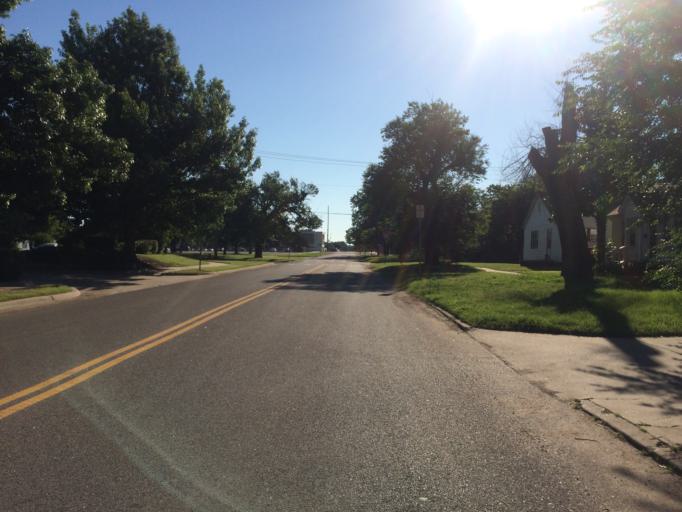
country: US
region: Oklahoma
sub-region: Cleveland County
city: Norman
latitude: 35.2180
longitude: -97.4448
